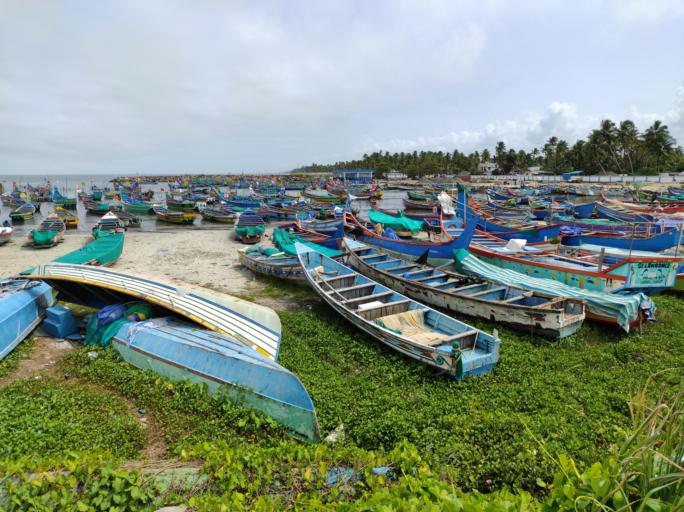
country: IN
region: Kerala
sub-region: Alappuzha
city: Kutiatodu
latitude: 9.7983
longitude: 76.2749
